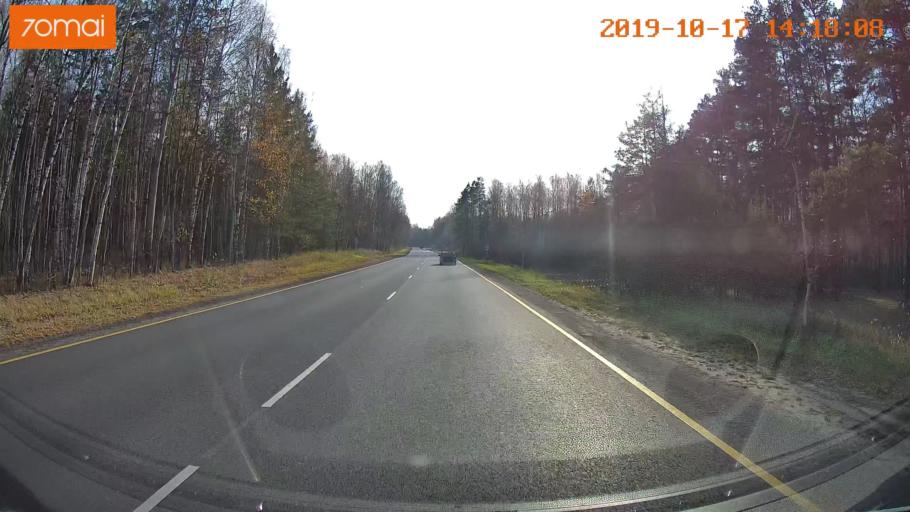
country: RU
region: Rjazan
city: Spas-Klepiki
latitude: 55.0672
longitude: 40.0328
